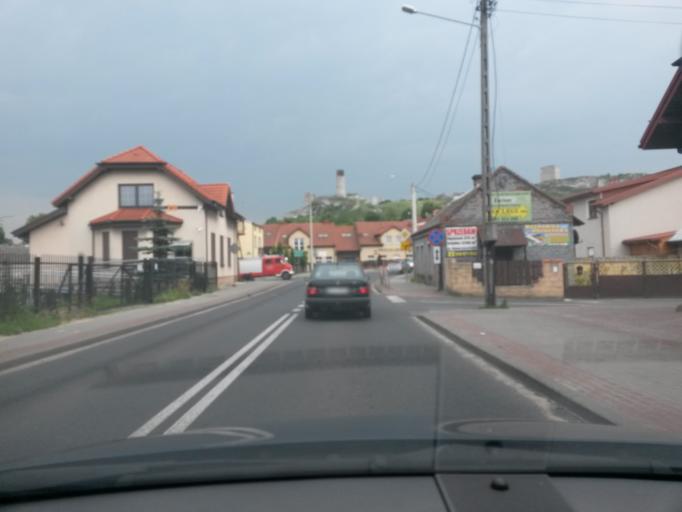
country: PL
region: Silesian Voivodeship
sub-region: Powiat czestochowski
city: Olsztyn
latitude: 50.7508
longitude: 19.2671
